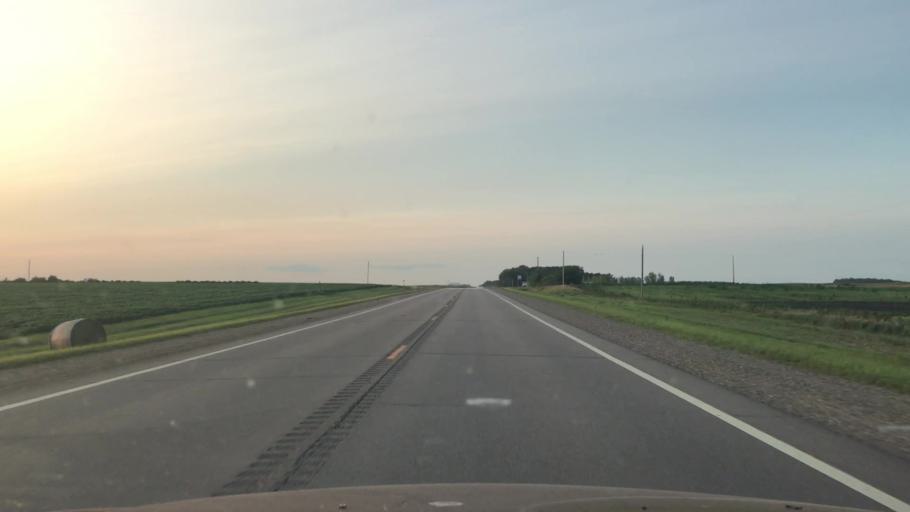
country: US
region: Minnesota
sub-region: Redwood County
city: Redwood Falls
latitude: 44.4390
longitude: -95.1176
